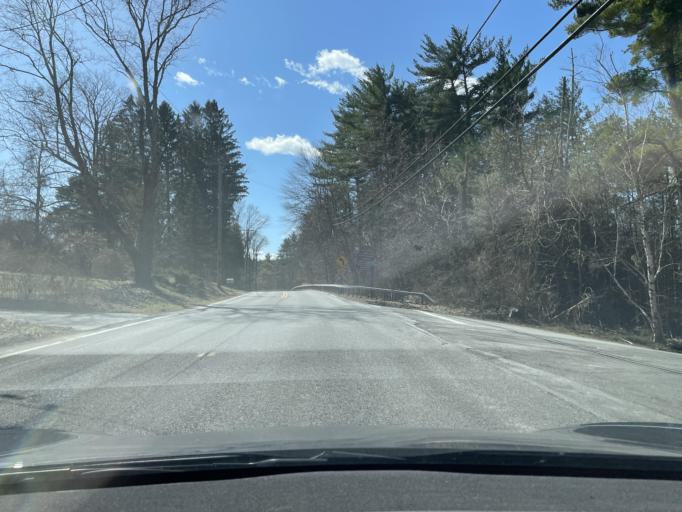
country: US
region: New York
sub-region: Ulster County
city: West Hurley
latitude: 42.0125
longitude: -74.1073
